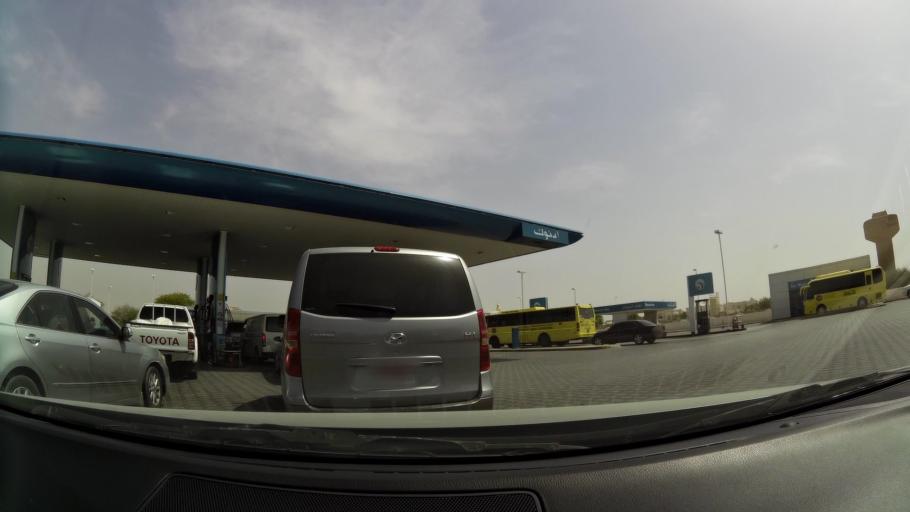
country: AE
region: Abu Dhabi
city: Al Ain
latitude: 24.1713
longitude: 55.7102
